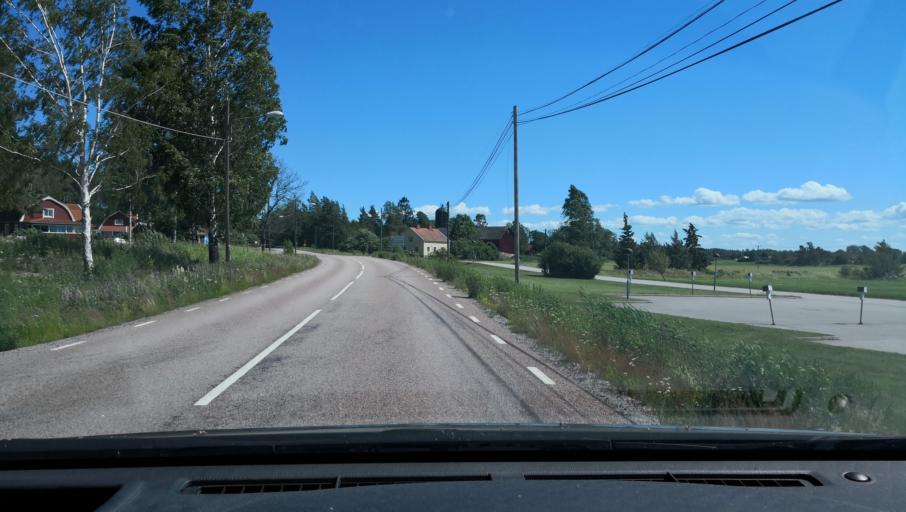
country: SE
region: Vaestmanland
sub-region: Arboga Kommun
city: Tyringe
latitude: 59.2930
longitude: 16.0480
